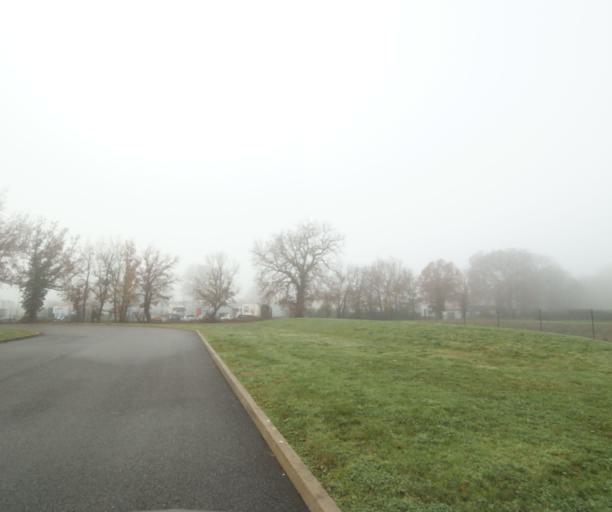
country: FR
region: Midi-Pyrenees
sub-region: Departement de la Haute-Garonne
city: Villemur-sur-Tarn
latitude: 43.8409
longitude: 1.4954
